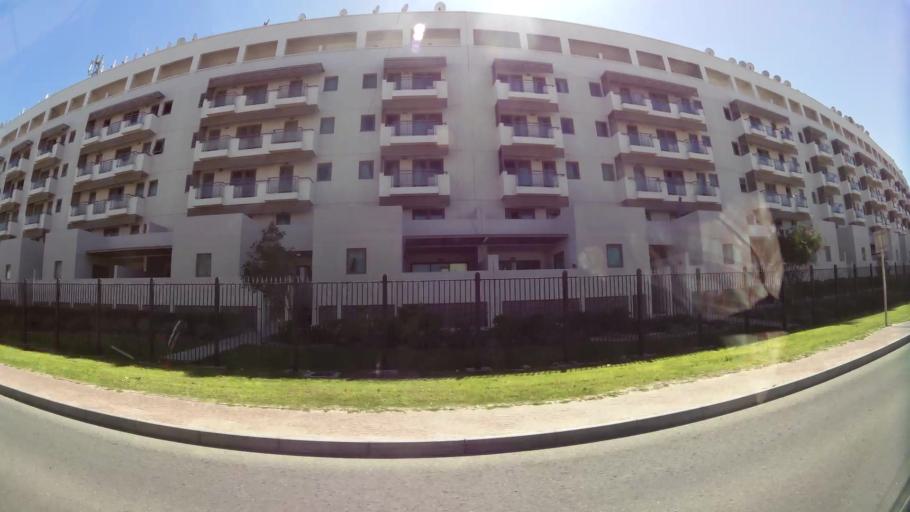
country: BH
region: Muharraq
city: Al Hadd
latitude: 26.3005
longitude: 50.6631
